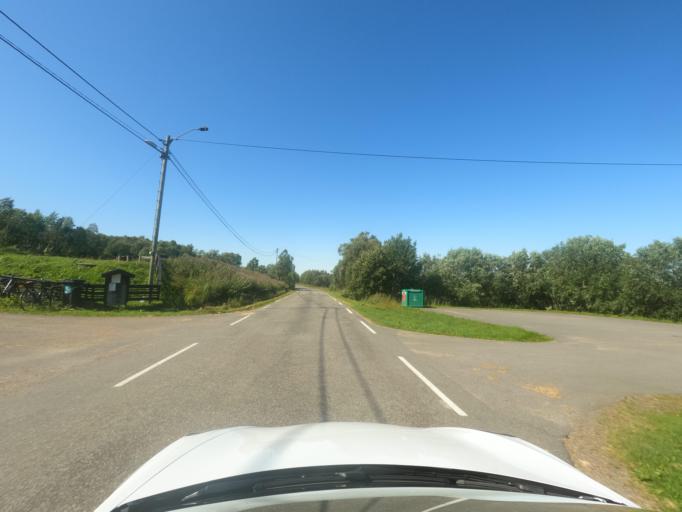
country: NO
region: Nordland
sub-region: Hadsel
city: Melbu
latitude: 68.4340
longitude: 14.7550
